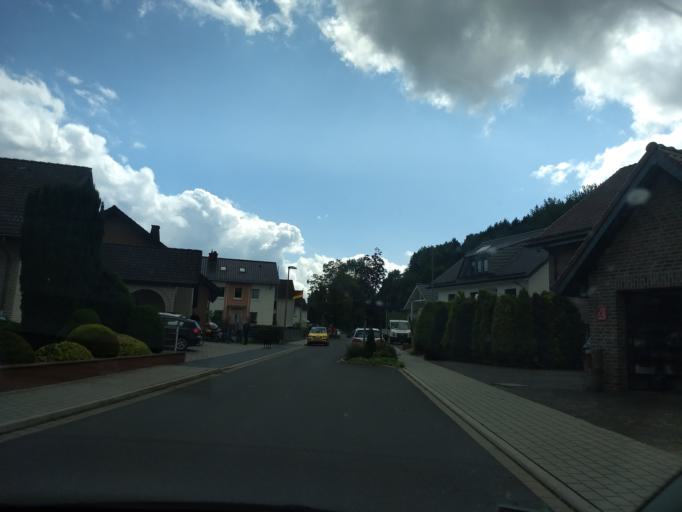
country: DE
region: North Rhine-Westphalia
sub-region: Regierungsbezirk Detmold
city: Buren
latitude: 51.5373
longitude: 8.5260
